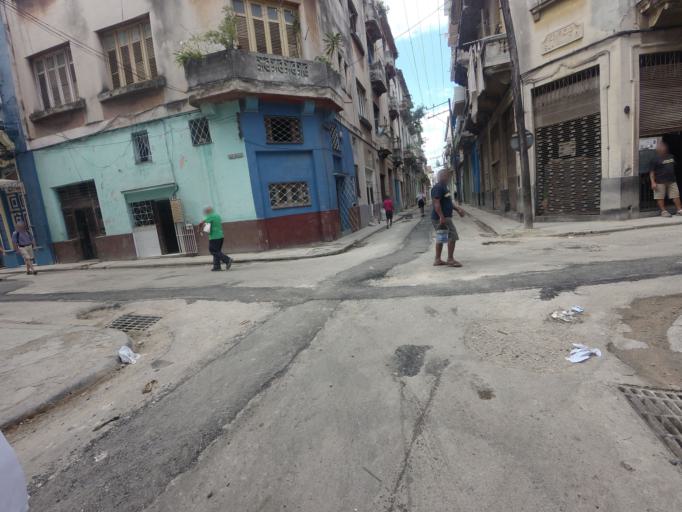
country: CU
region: La Habana
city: La Habana Vieja
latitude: 23.1323
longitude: -82.3490
